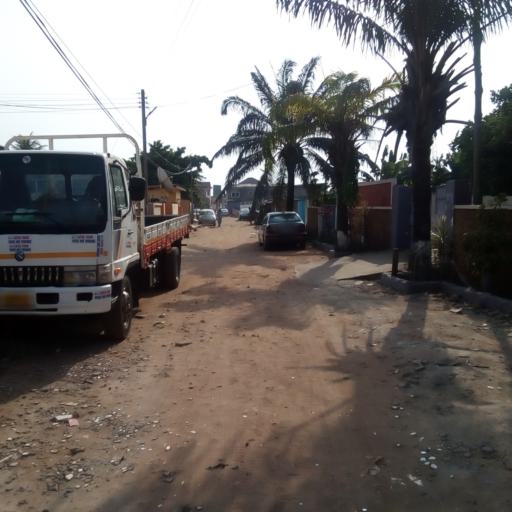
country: GH
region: Greater Accra
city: Accra
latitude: 5.5878
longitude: -0.2152
